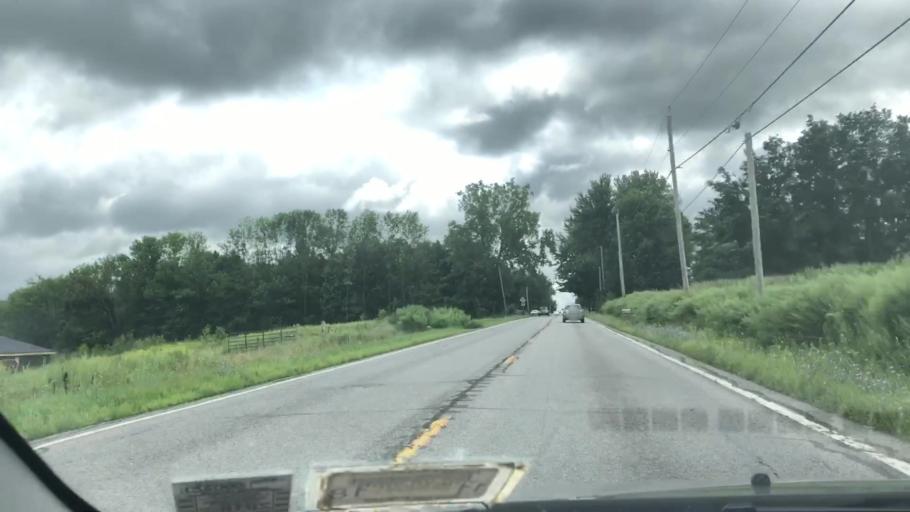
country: US
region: New York
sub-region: Wayne County
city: Macedon
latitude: 43.1138
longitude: -77.2932
